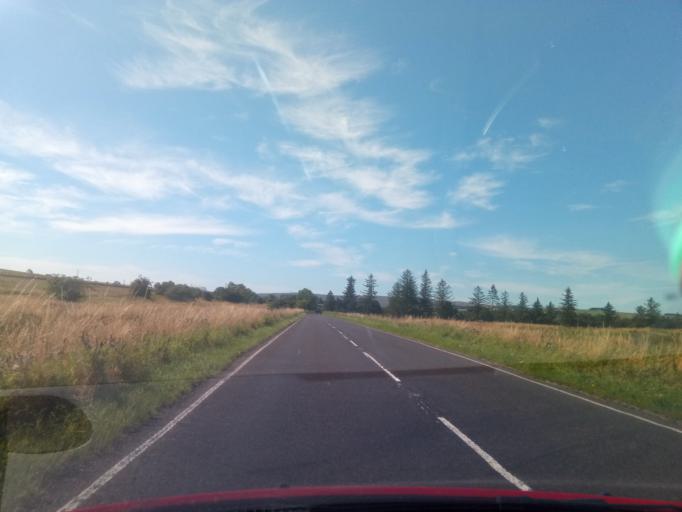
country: GB
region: England
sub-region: Northumberland
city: Bardon Mill
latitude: 54.9369
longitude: -2.2893
